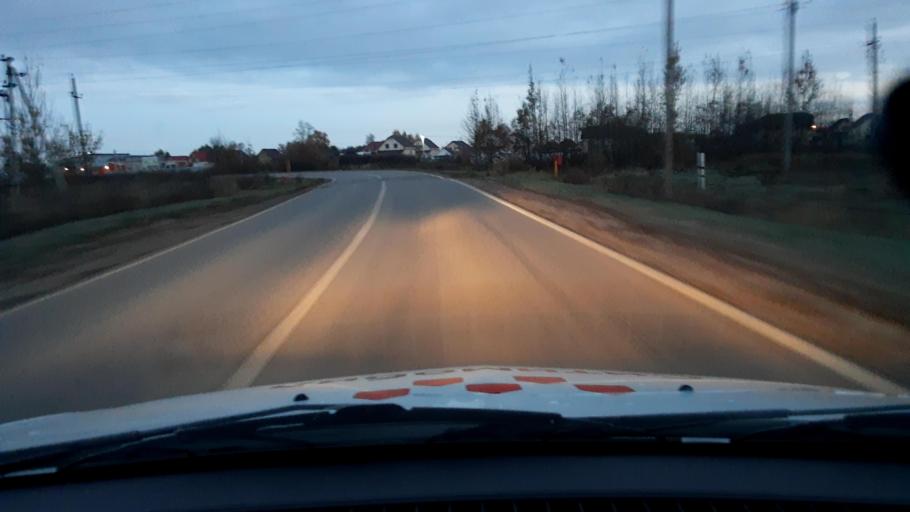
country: RU
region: Bashkortostan
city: Kabakovo
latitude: 54.7435
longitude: 56.2021
